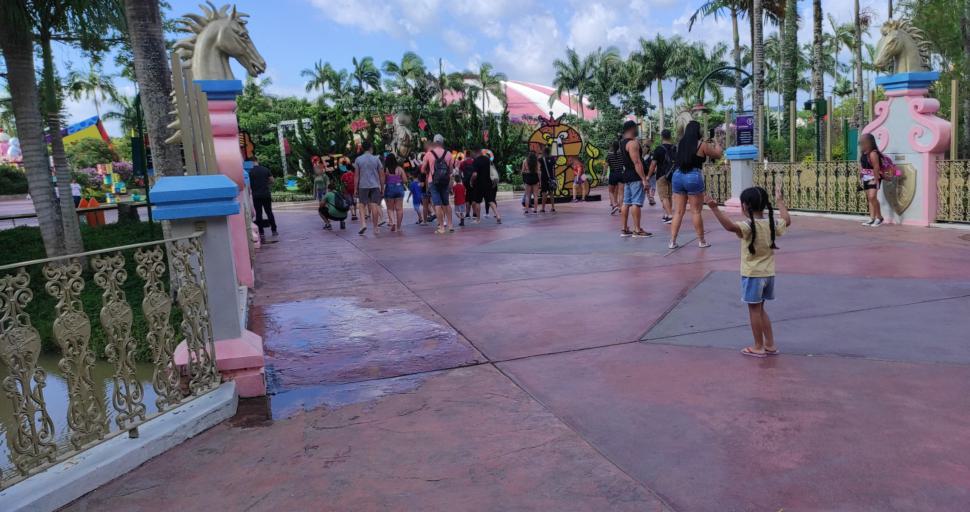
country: BR
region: Santa Catarina
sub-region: Penha
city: Penha
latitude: -26.8005
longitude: -48.6136
